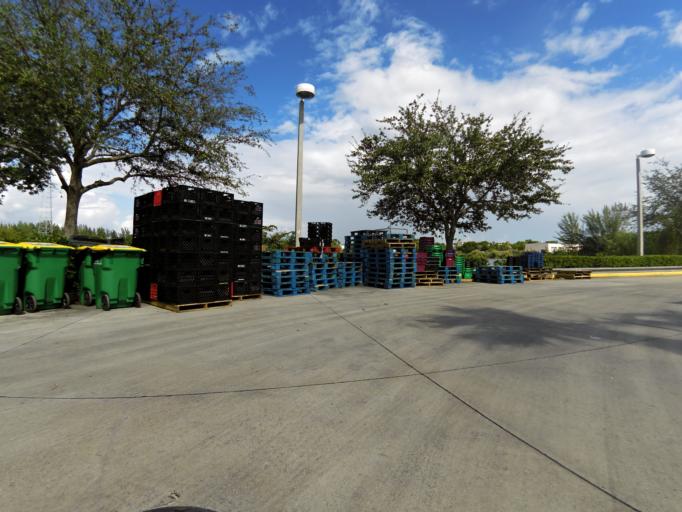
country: US
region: Florida
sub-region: Broward County
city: Davie
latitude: 26.0876
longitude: -80.2312
